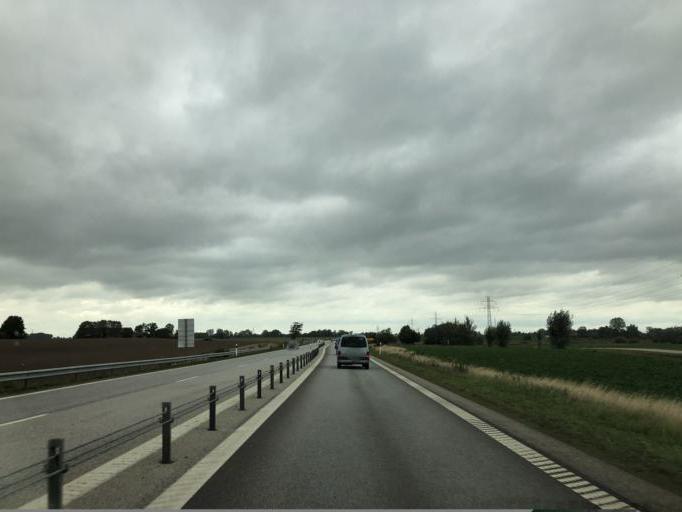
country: SE
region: Skane
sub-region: Lunds Kommun
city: Lund
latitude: 55.7302
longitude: 13.1475
